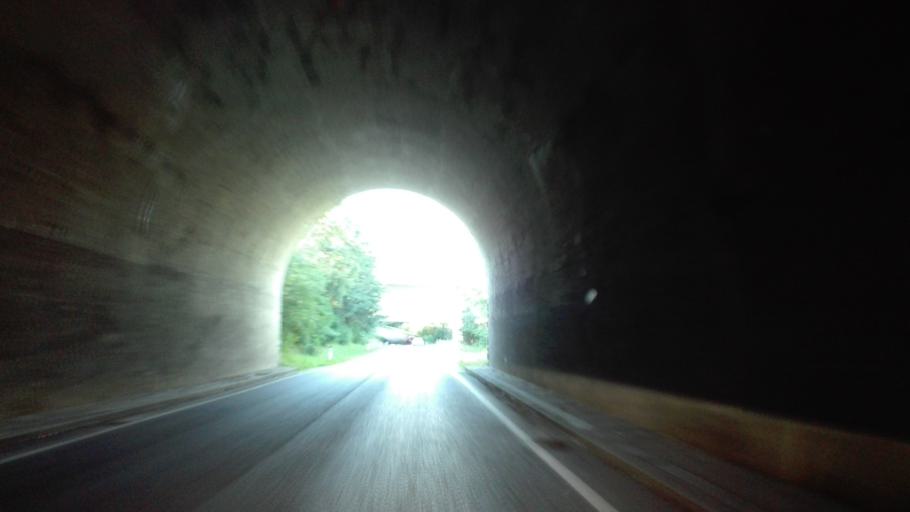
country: AT
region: Lower Austria
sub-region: Politischer Bezirk Sankt Polten
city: Eichgraben
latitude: 48.1515
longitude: 15.9719
